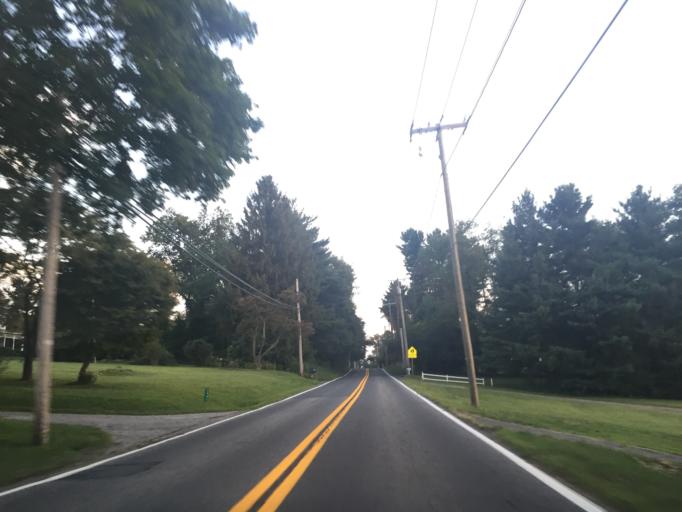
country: US
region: Maryland
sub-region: Harford County
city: Bel Air North
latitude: 39.5902
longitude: -76.3879
